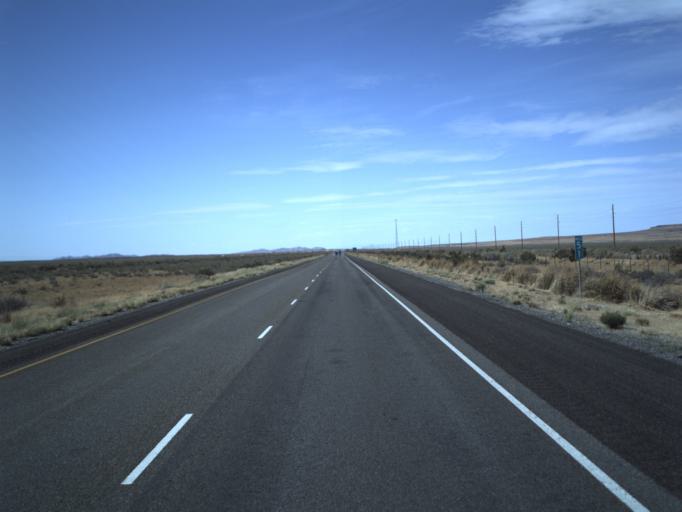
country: US
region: Utah
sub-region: Tooele County
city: Grantsville
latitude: 40.7426
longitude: -113.0767
